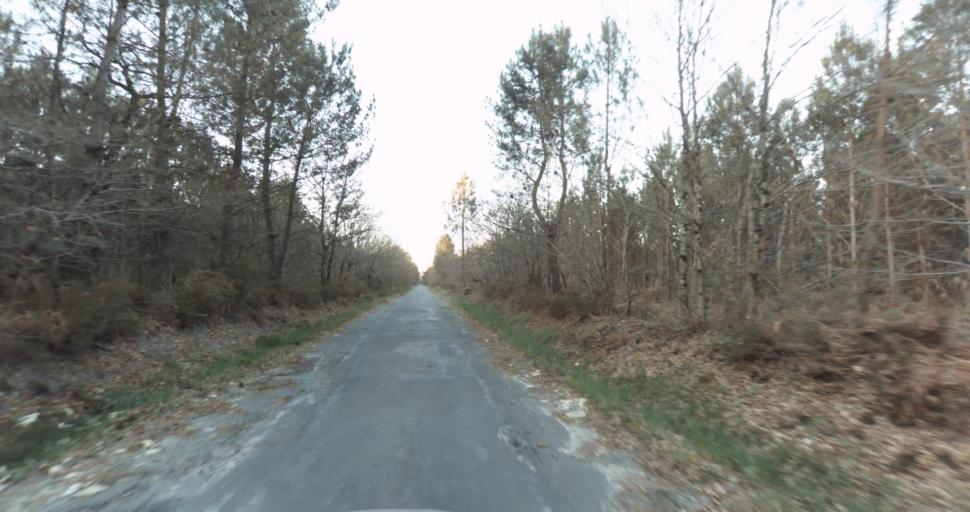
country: FR
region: Aquitaine
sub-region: Departement de la Gironde
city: Martignas-sur-Jalle
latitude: 44.8256
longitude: -0.7407
